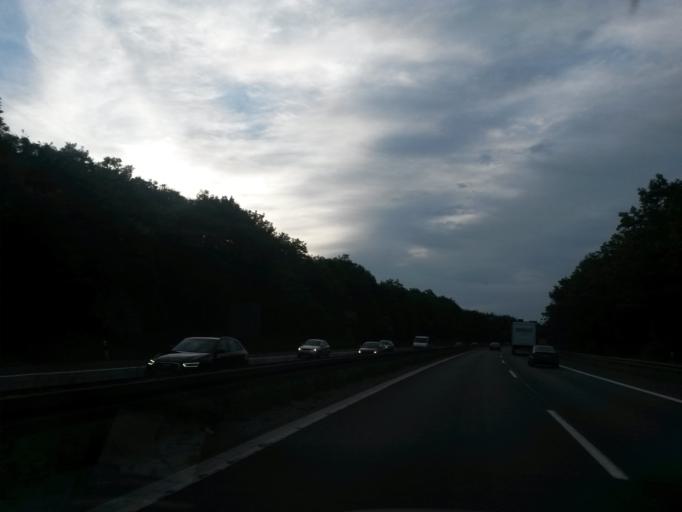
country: DE
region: Bavaria
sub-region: Regierungsbezirk Mittelfranken
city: Wendelstein
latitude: 49.3951
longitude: 11.1047
